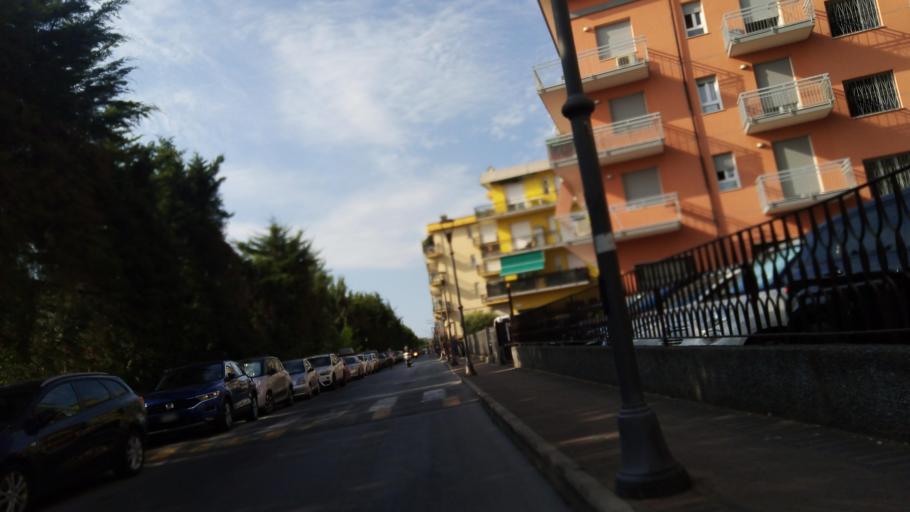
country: IT
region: Liguria
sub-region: Provincia di Savona
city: Ceriale
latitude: 44.0892
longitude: 8.2289
